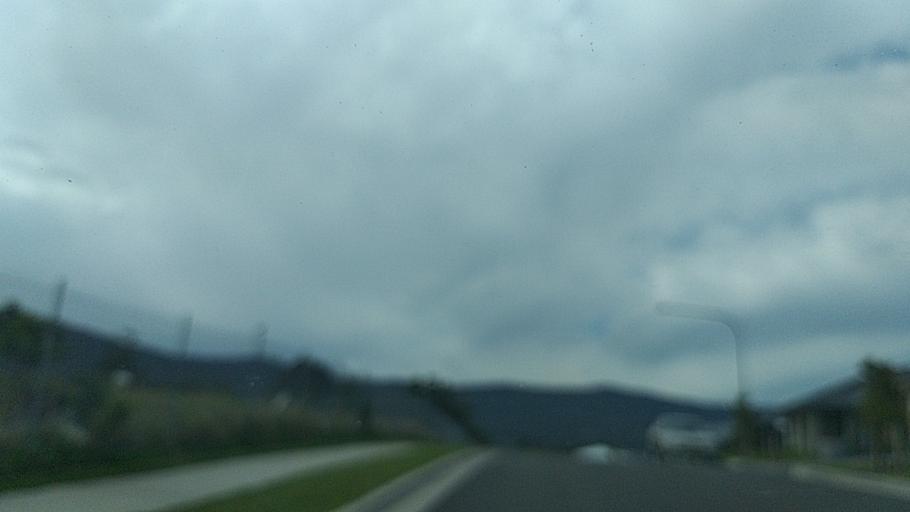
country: AU
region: New South Wales
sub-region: Wollongong
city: Dapto
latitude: -34.4967
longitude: 150.7565
